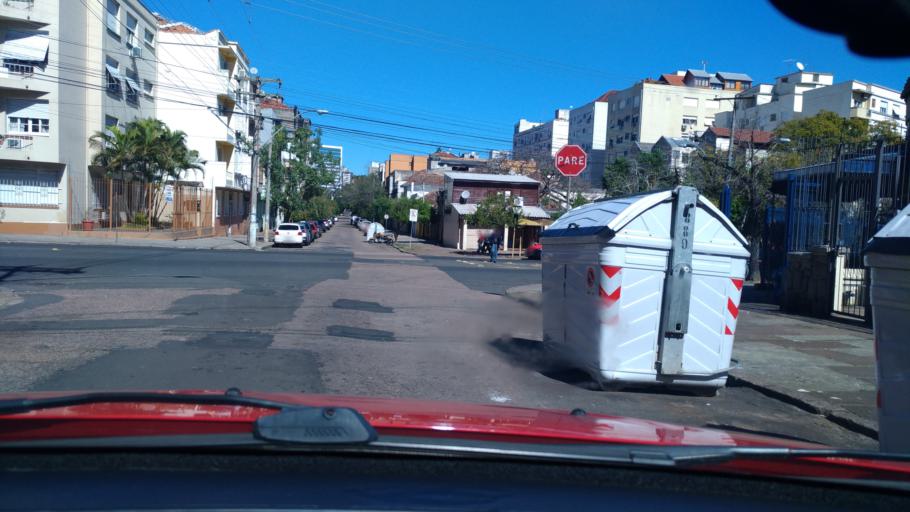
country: BR
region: Rio Grande do Sul
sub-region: Porto Alegre
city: Porto Alegre
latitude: -30.0401
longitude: -51.2092
